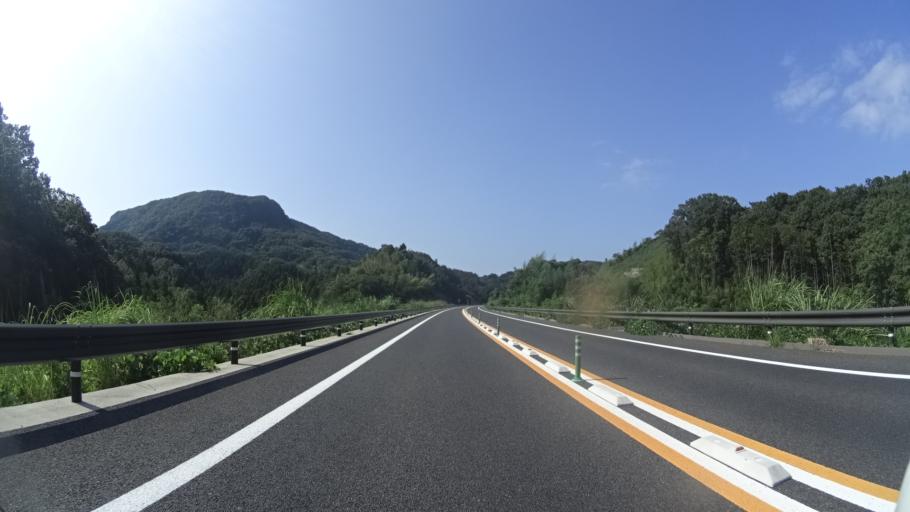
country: JP
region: Shimane
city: Odacho-oda
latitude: 35.0993
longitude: 132.3766
